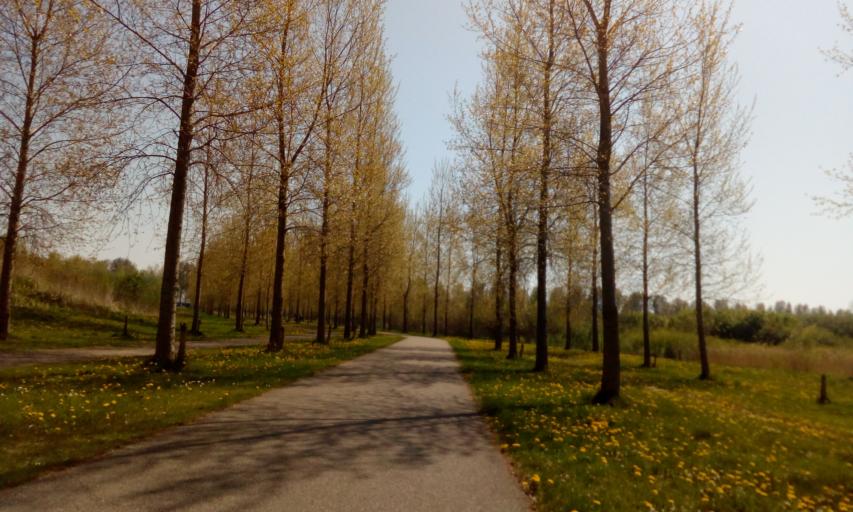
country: NL
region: South Holland
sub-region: Gemeente Hillegom
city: Hillegom
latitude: 52.2579
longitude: 4.6170
